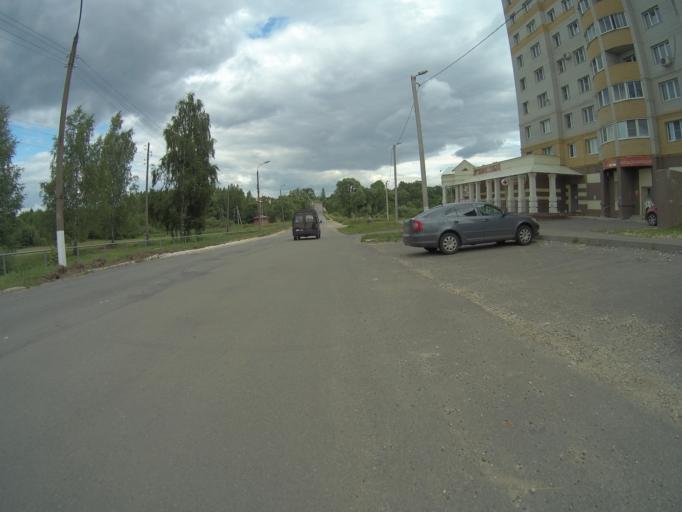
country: RU
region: Vladimir
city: Kommunar
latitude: 56.0627
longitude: 40.4873
